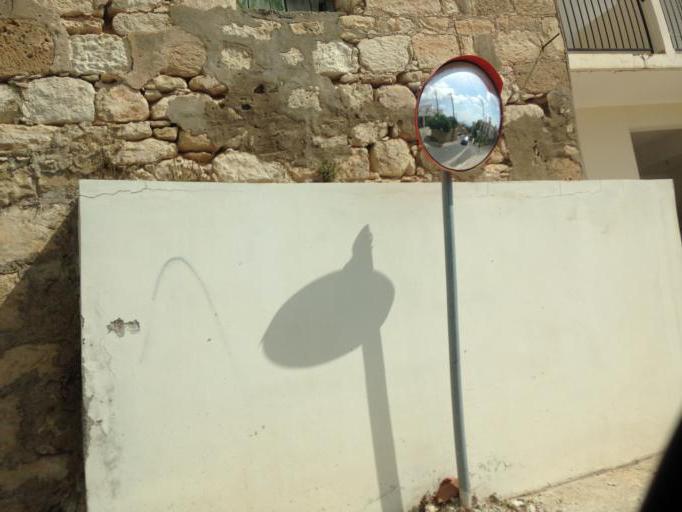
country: CY
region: Pafos
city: Pegeia
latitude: 34.8854
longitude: 32.3829
